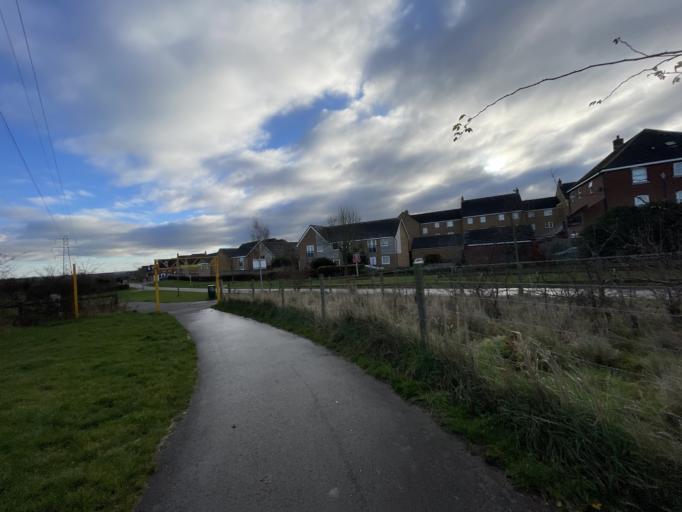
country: GB
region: England
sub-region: Warwickshire
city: Rugby
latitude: 52.3996
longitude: -1.2391
